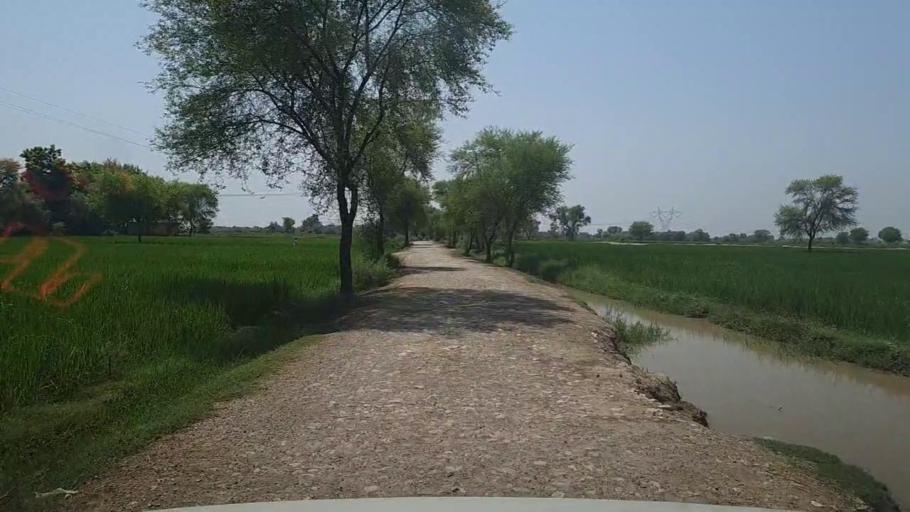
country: PK
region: Sindh
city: Kandhkot
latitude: 28.3165
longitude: 69.3627
